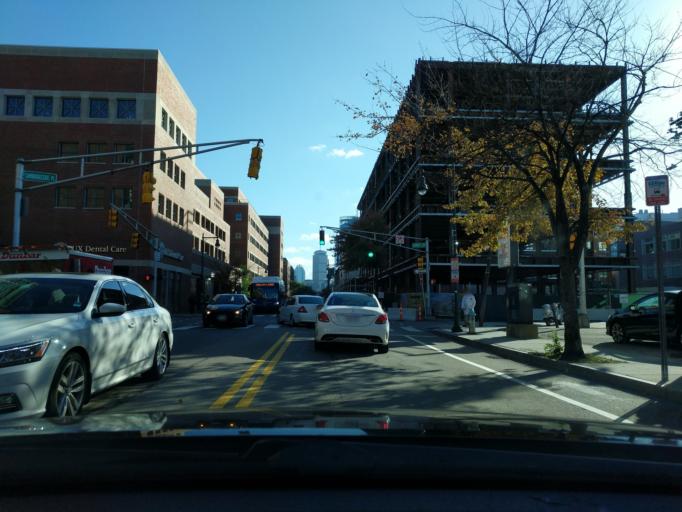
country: US
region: Massachusetts
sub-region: Suffolk County
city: Boston
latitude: 42.3676
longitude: -71.0777
